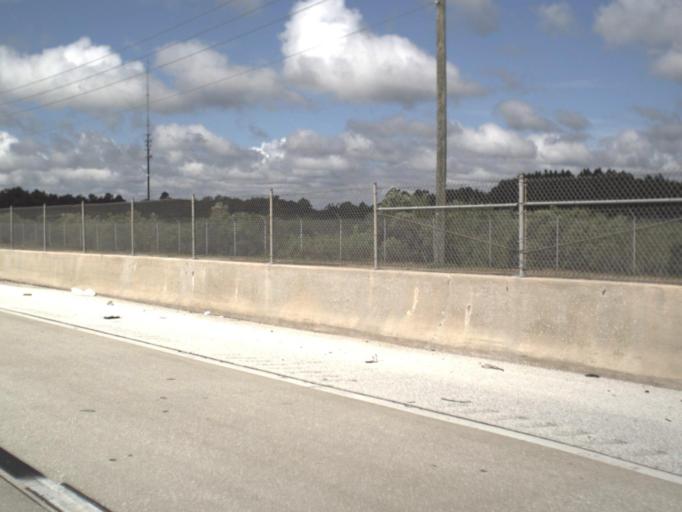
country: US
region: Florida
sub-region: Polk County
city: Winston
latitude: 28.0464
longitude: -82.0232
